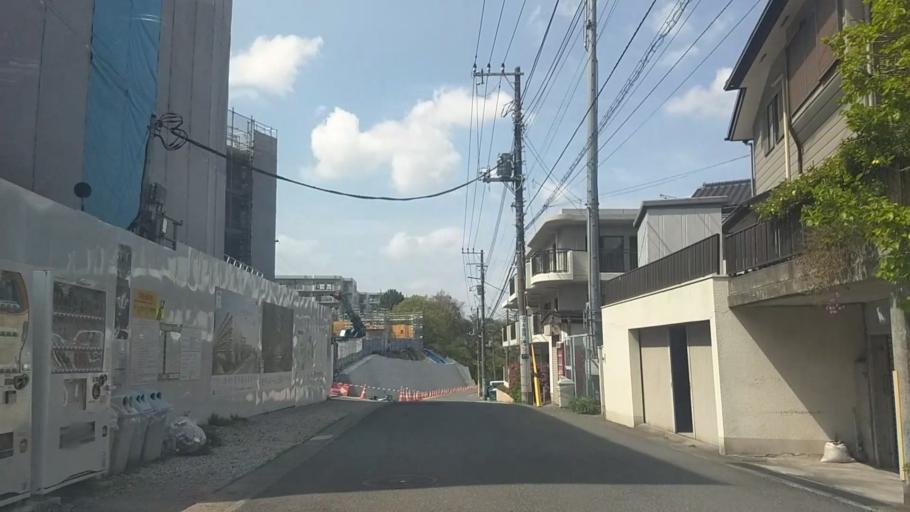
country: JP
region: Kanagawa
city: Kamakura
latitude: 35.3748
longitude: 139.5714
